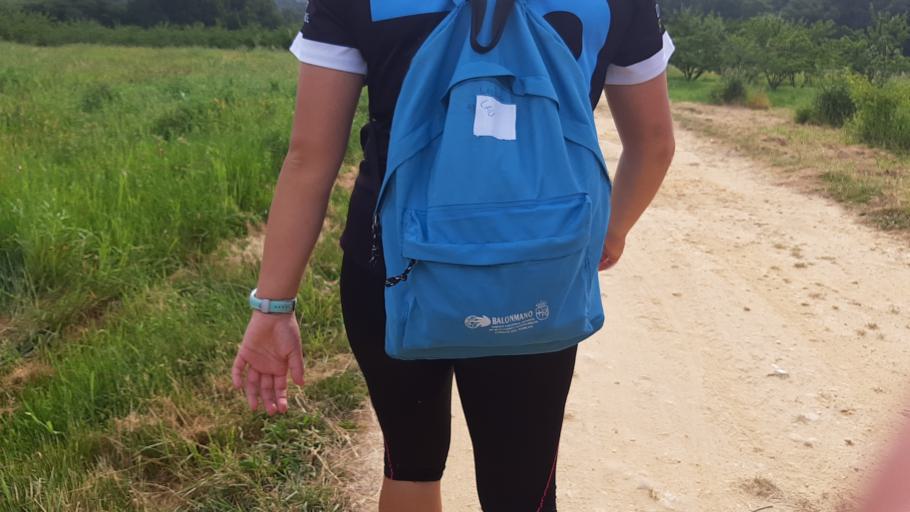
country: ES
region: Galicia
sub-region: Provincia de Pontevedra
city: O Rosal
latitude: 41.9247
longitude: -8.8291
